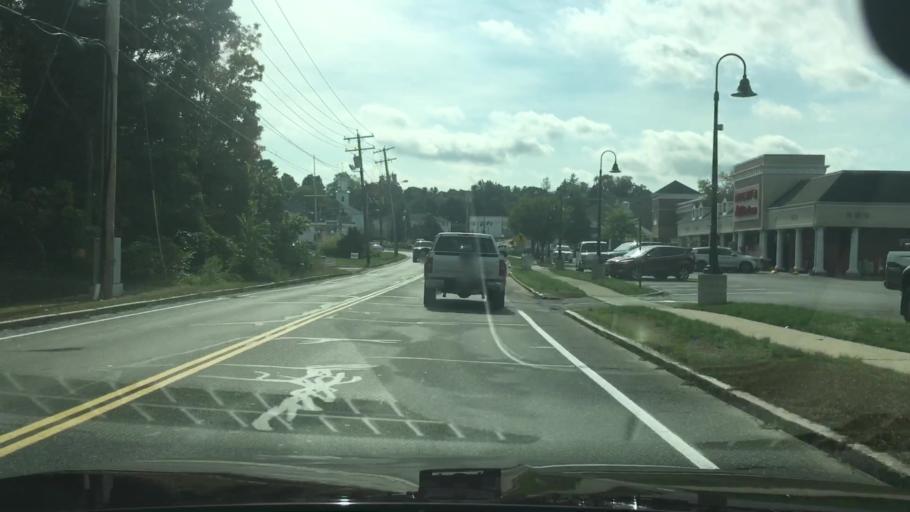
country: US
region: Massachusetts
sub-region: Hampden County
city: East Longmeadow
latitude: 42.0668
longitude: -72.5141
